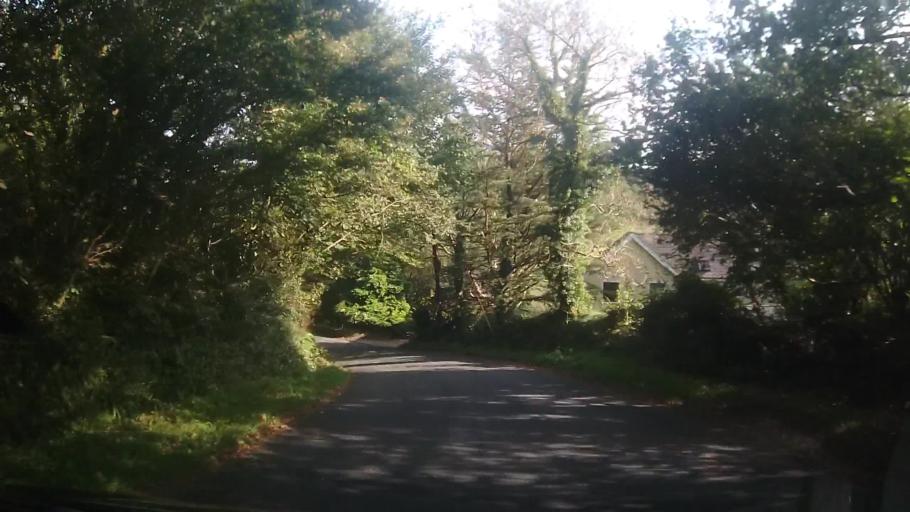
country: GB
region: Wales
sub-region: Pembrokeshire
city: Fishguard
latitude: 51.9844
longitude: -4.9535
